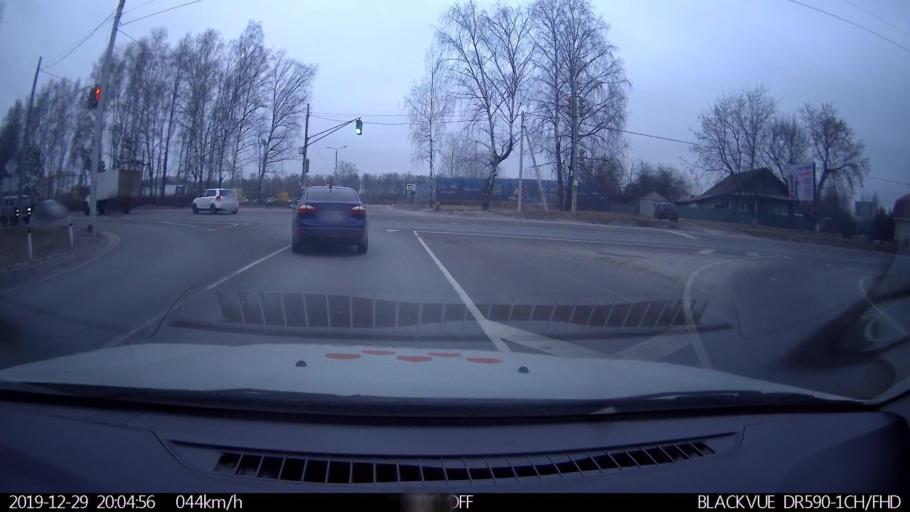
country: RU
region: Nizjnij Novgorod
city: Neklyudovo
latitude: 56.3878
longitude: 44.0109
